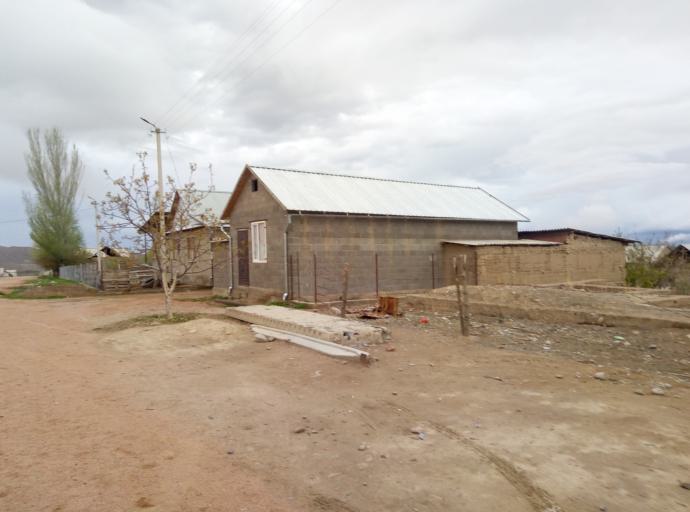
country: KG
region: Ysyk-Koel
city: Bokombayevskoye
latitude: 42.1093
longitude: 76.9787
